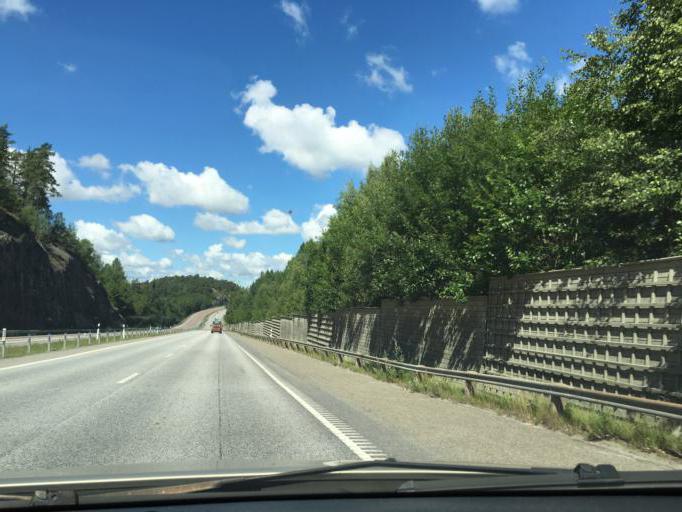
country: SE
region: Stockholm
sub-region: Nacka Kommun
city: Nacka
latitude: 59.2994
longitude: 18.1946
